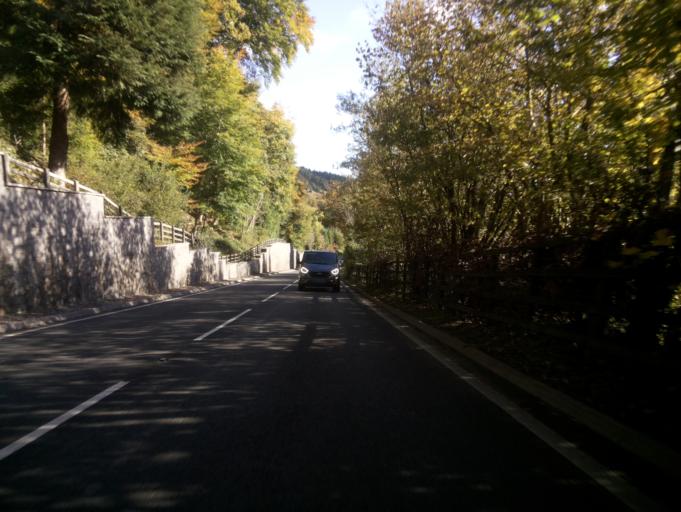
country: GB
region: Wales
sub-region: Rhondda Cynon Taf
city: Hirwaun
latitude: 51.8265
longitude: -3.4519
